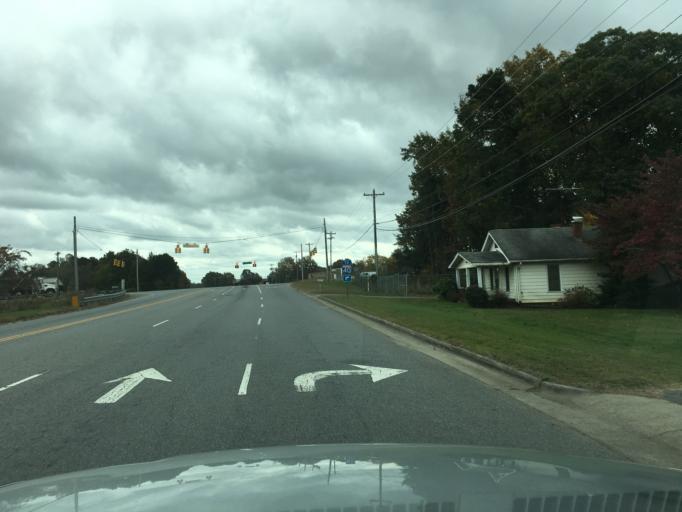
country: US
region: North Carolina
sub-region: Catawba County
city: Saint Stephens
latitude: 35.7232
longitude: -81.2947
